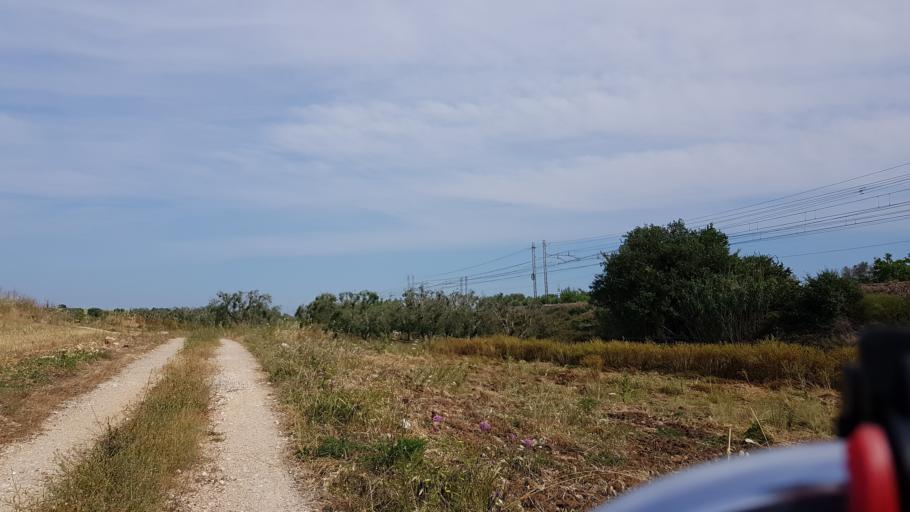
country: IT
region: Apulia
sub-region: Provincia di Brindisi
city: San Vito dei Normanni
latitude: 40.6592
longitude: 17.7996
